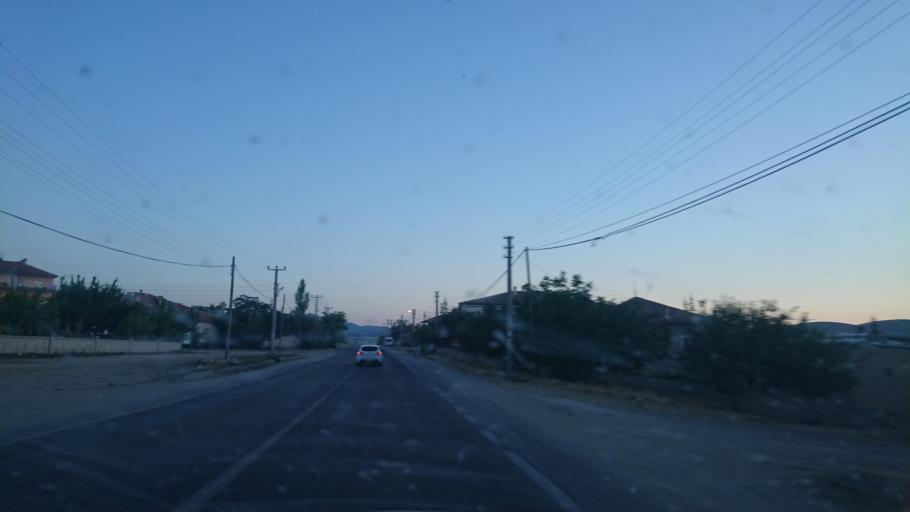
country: TR
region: Aksaray
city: Balci
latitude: 38.7908
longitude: 34.1228
